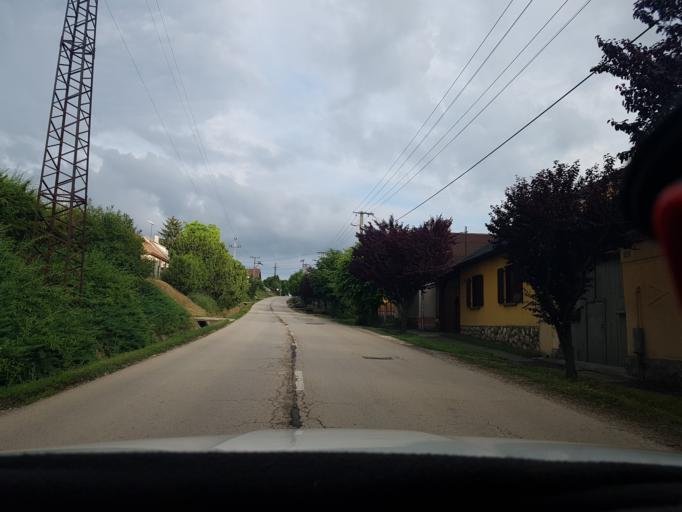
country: HU
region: Komarom-Esztergom
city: Sarisap
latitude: 47.6712
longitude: 18.6863
